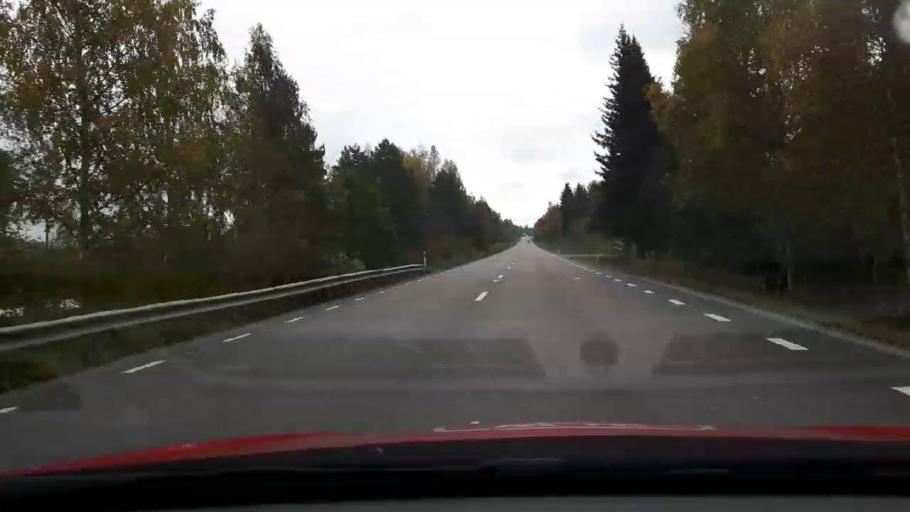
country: SE
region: Gaevleborg
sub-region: Bollnas Kommun
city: Kilafors
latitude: 61.2949
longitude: 16.4938
